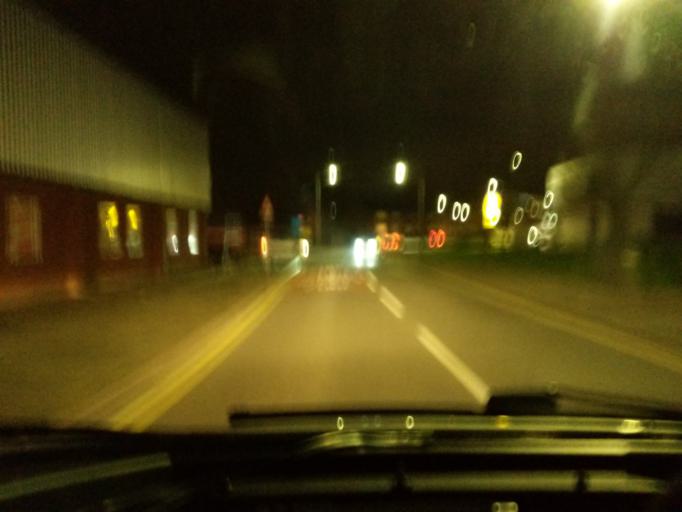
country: GB
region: England
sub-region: St. Helens
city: St Helens
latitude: 53.4544
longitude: -2.7427
